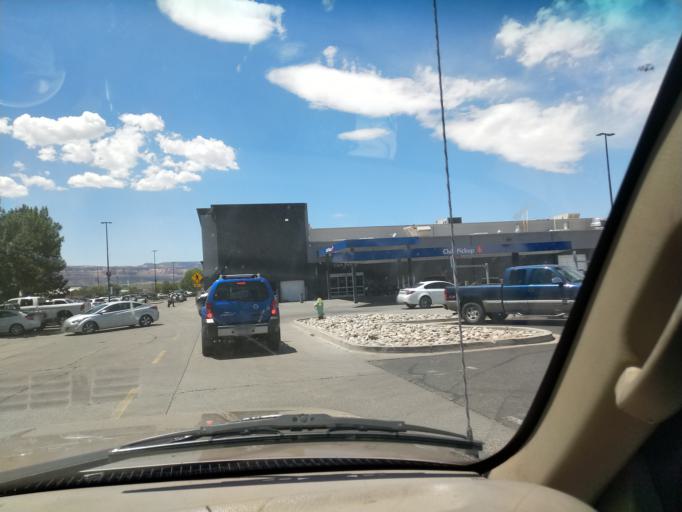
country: US
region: Colorado
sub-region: Mesa County
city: Grand Junction
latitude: 39.0826
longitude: -108.5820
